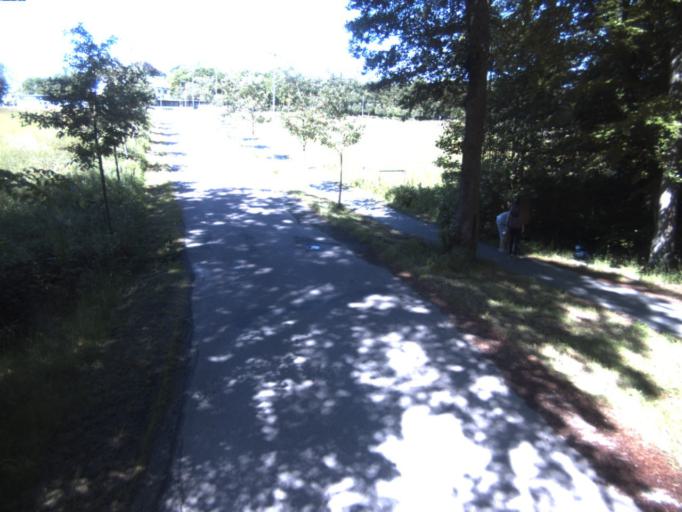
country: SE
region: Skane
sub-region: Helsingborg
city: Helsingborg
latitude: 56.0707
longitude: 12.6784
